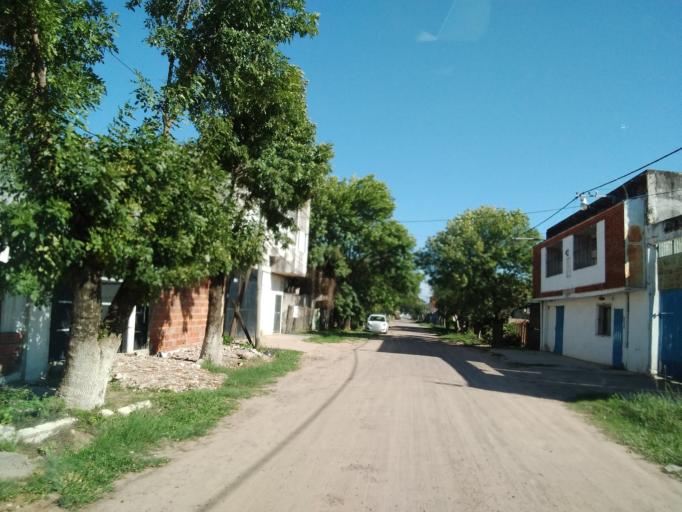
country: AR
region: Corrientes
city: Corrientes
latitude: -27.4840
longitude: -58.8034
